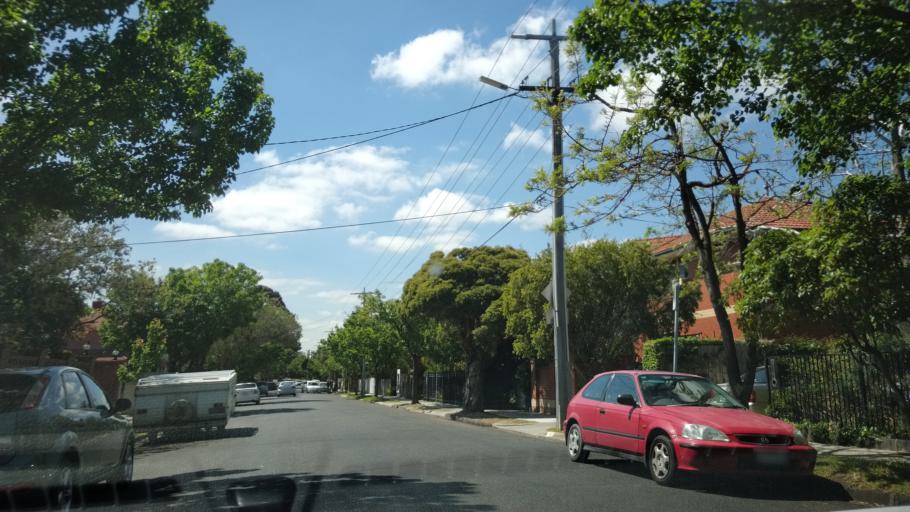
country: AU
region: Victoria
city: Ormond
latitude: -37.8965
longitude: 145.0377
